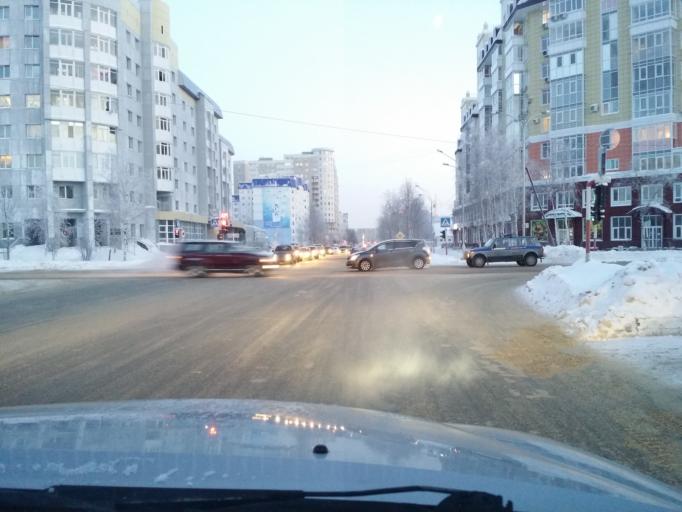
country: RU
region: Khanty-Mansiyskiy Avtonomnyy Okrug
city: Nizhnevartovsk
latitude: 60.9362
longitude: 76.5733
